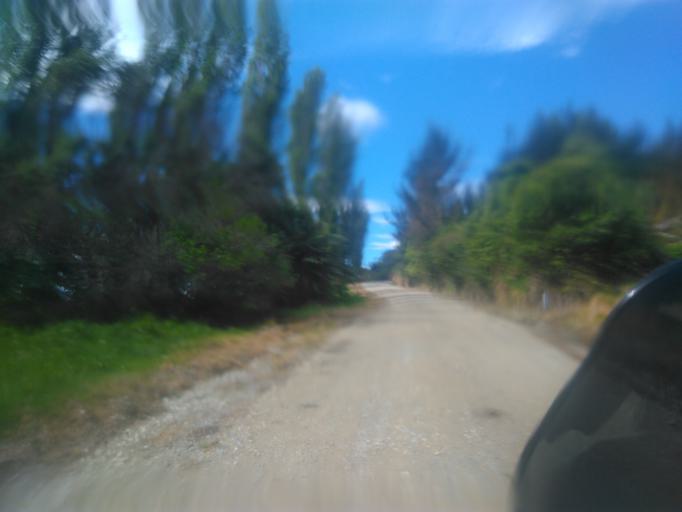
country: NZ
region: Hawke's Bay
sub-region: Wairoa District
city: Wairoa
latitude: -38.7709
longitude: 177.6006
